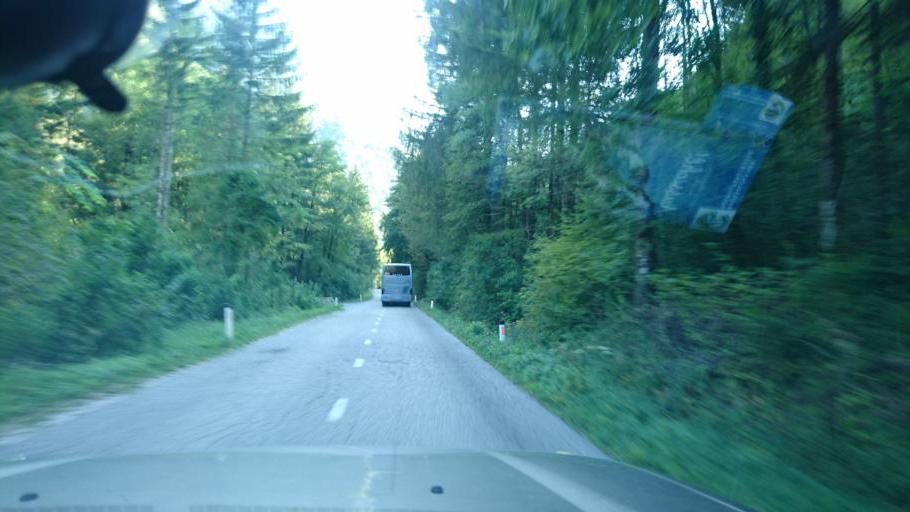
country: SI
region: Bovec
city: Bovec
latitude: 46.3365
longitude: 13.5982
